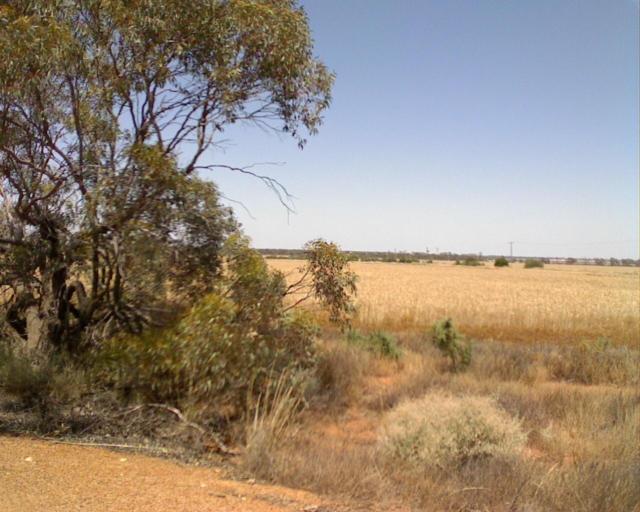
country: AU
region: Western Australia
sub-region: Wongan-Ballidu
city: Wongan Hills
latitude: -30.4520
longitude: 117.5257
